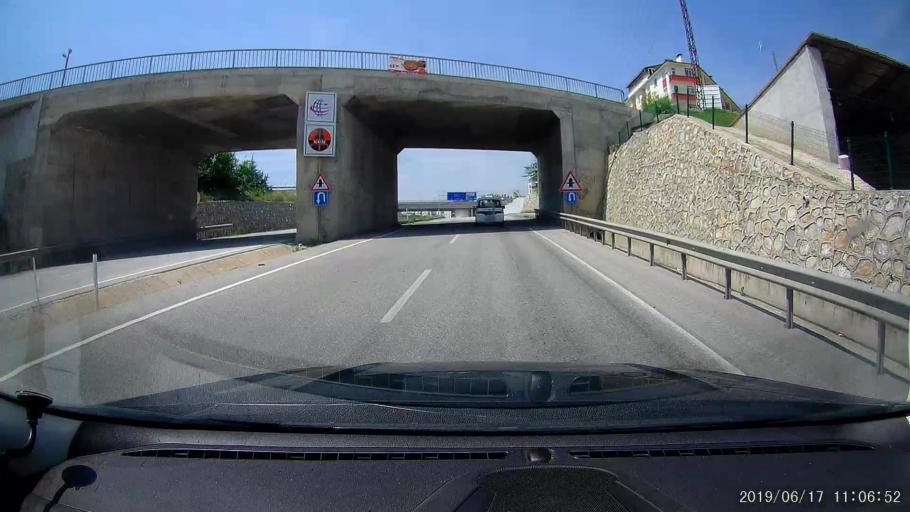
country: TR
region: Kastamonu
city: Tosya
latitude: 41.0091
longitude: 34.0609
